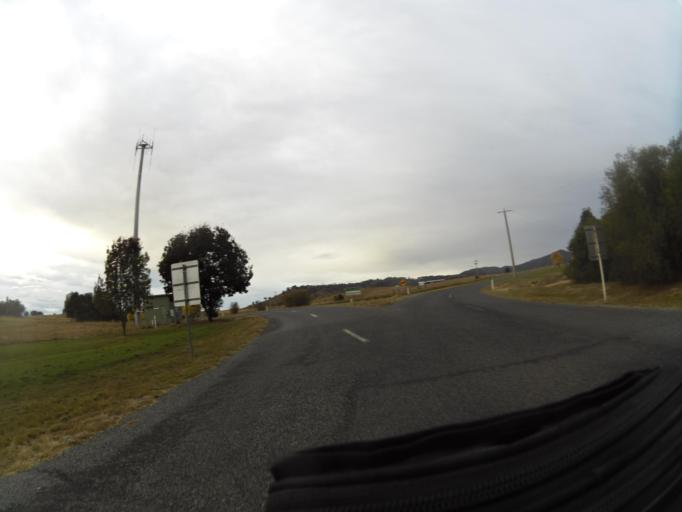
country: AU
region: New South Wales
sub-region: Greater Hume Shire
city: Holbrook
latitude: -36.0488
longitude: 147.9310
